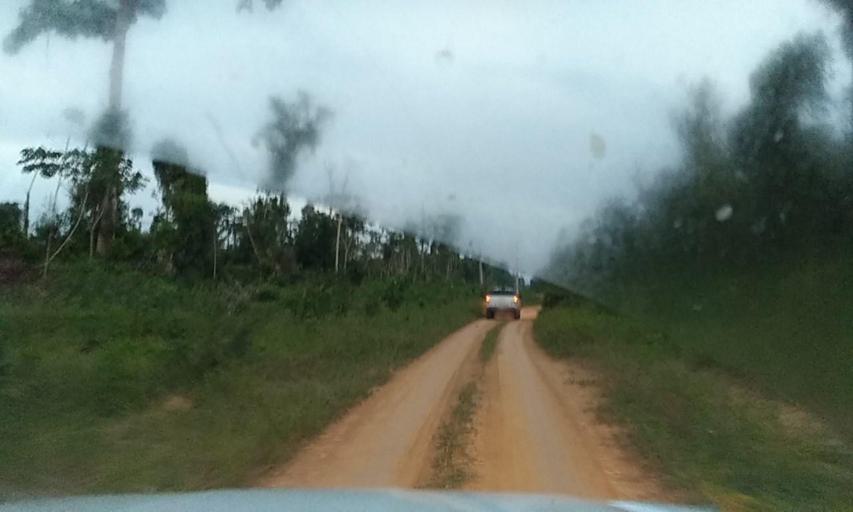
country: BR
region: Para
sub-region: Senador Jose Porfirio
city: Senador Jose Porfirio
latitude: -2.8945
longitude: -51.6882
